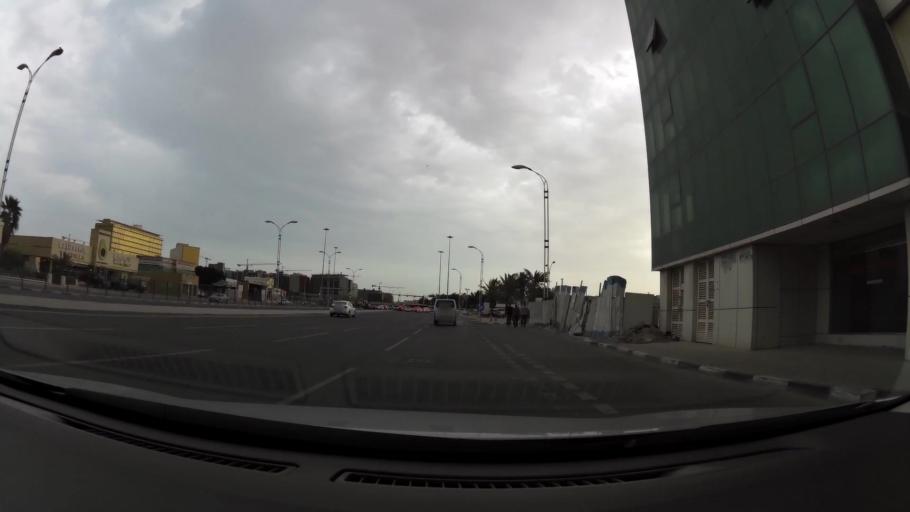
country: QA
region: Baladiyat ad Dawhah
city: Doha
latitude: 25.2737
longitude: 51.5095
